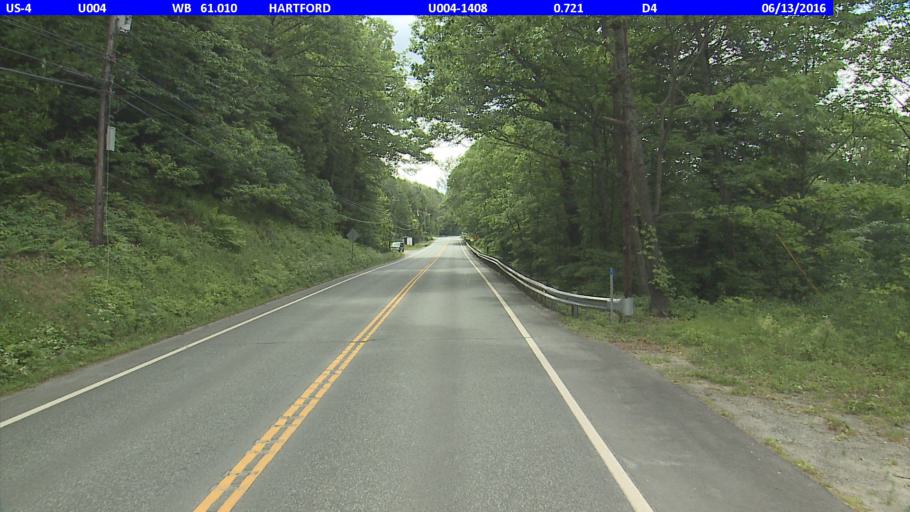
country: US
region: Vermont
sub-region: Windsor County
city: White River Junction
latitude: 43.6635
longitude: -72.3654
